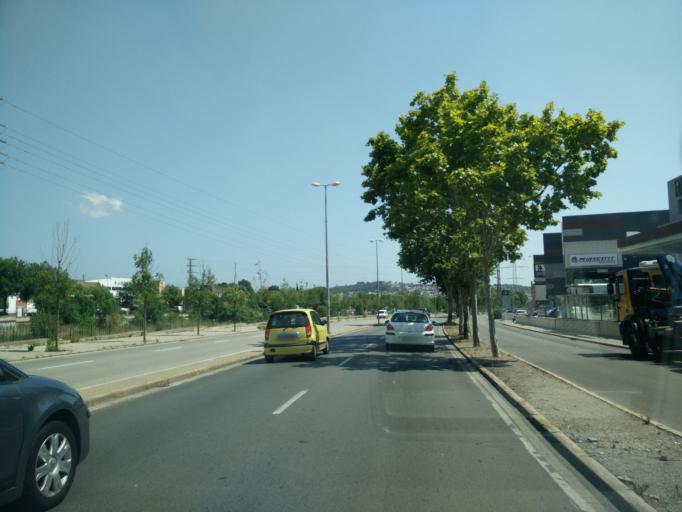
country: ES
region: Catalonia
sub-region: Provincia de Barcelona
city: Terrassa
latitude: 41.5518
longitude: 2.0383
